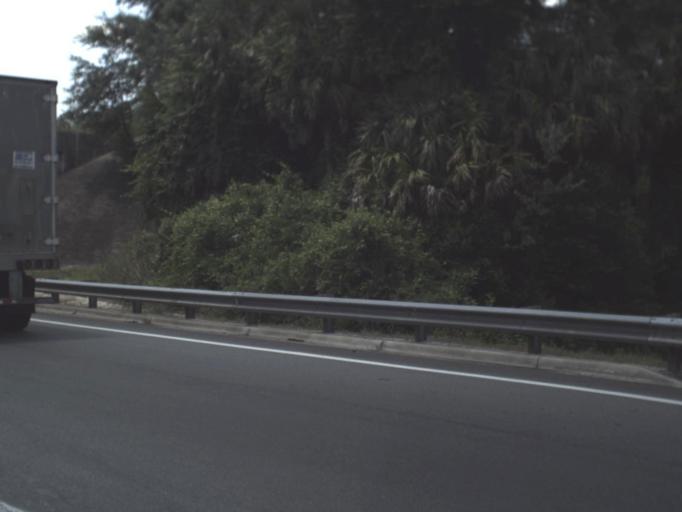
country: US
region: Florida
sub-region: Duval County
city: Baldwin
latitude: 30.2896
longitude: -81.9830
